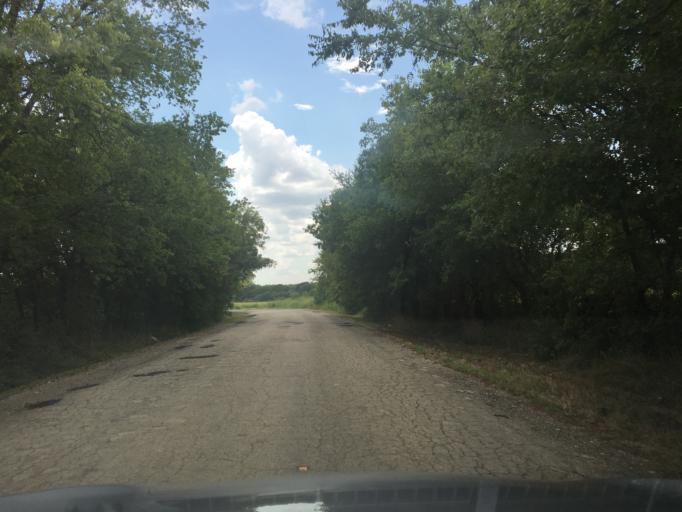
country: US
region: Texas
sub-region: Denton County
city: Denton
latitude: 33.1762
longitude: -97.1661
